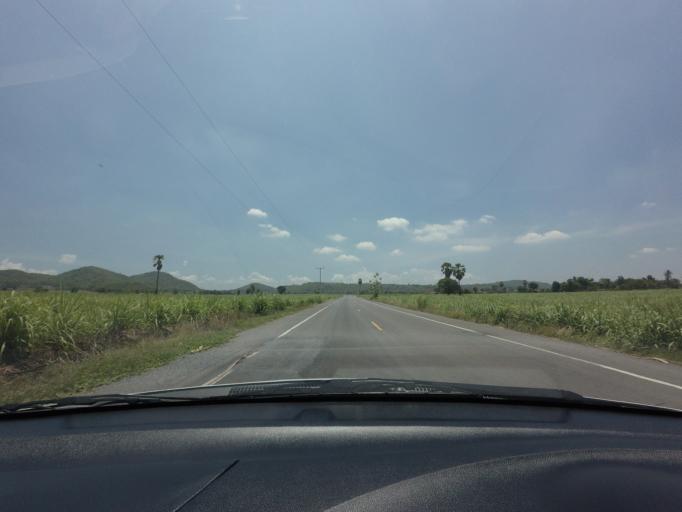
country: TH
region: Suphan Buri
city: Dan Chang
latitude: 14.9030
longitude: 99.7131
